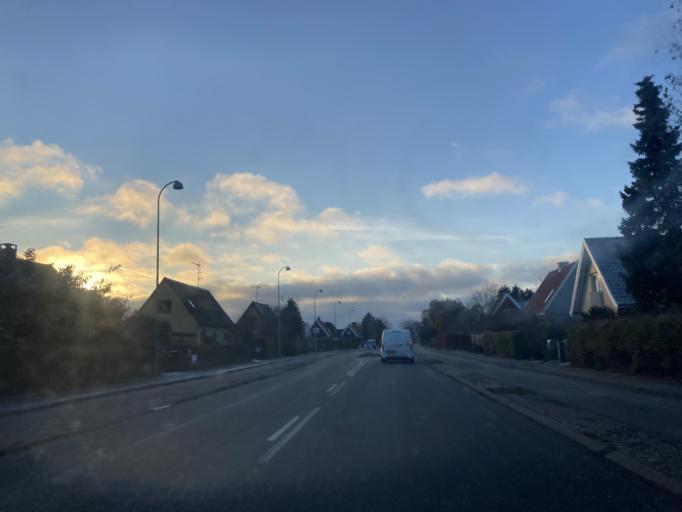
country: DK
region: Capital Region
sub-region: Hvidovre Kommune
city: Hvidovre
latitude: 55.6366
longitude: 12.4741
